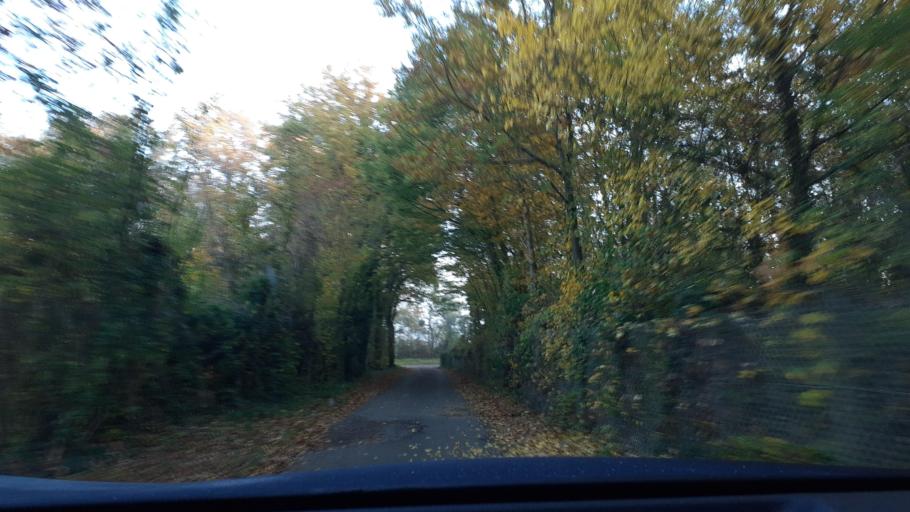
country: FR
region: Rhone-Alpes
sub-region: Departement du Rhone
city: Charnay
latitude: 45.9147
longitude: 4.6672
